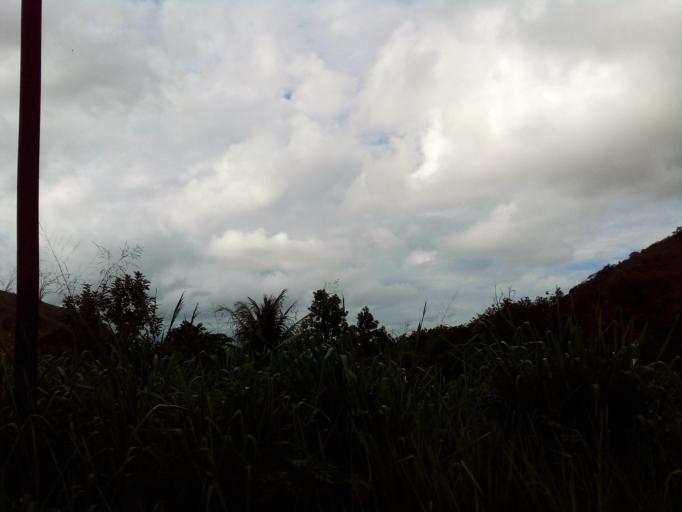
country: BR
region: Espirito Santo
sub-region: Joao Neiva
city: Joao Neiva
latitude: -19.6902
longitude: -40.3901
